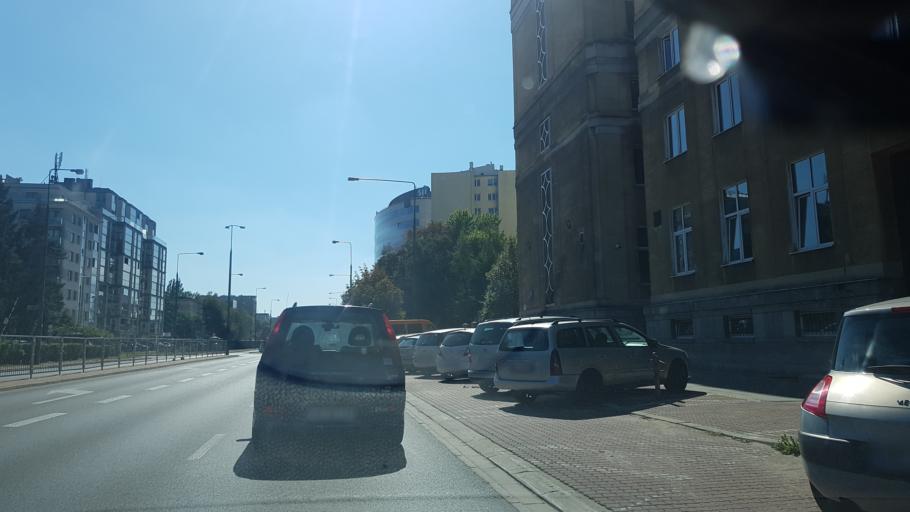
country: PL
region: Masovian Voivodeship
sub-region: Warszawa
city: Mokotow
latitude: 52.1925
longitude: 21.0153
